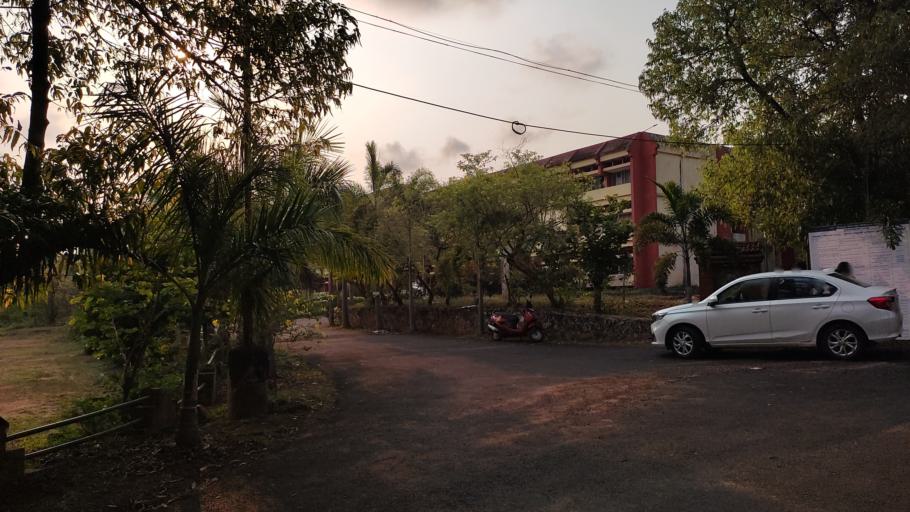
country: IN
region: Kerala
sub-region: Malappuram
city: Tirur
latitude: 10.8522
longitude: 75.9865
